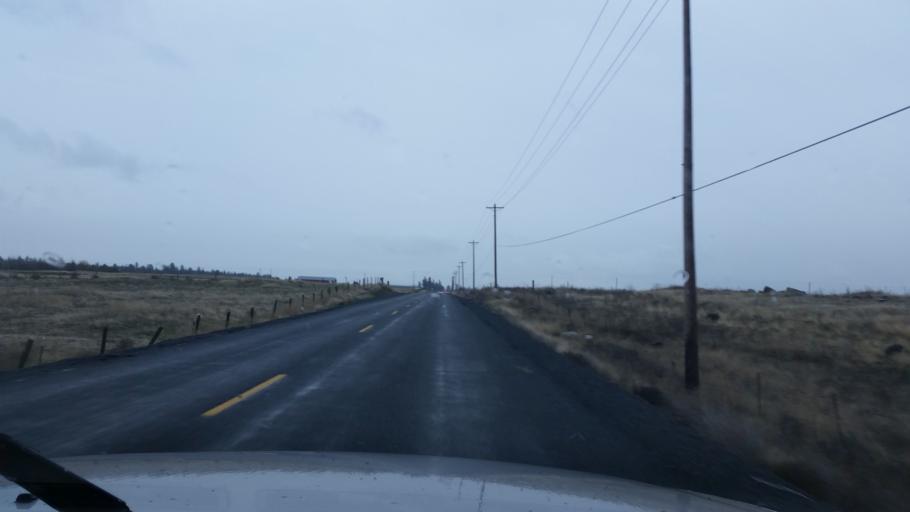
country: US
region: Washington
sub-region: Spokane County
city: Airway Heights
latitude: 47.6718
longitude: -117.5683
